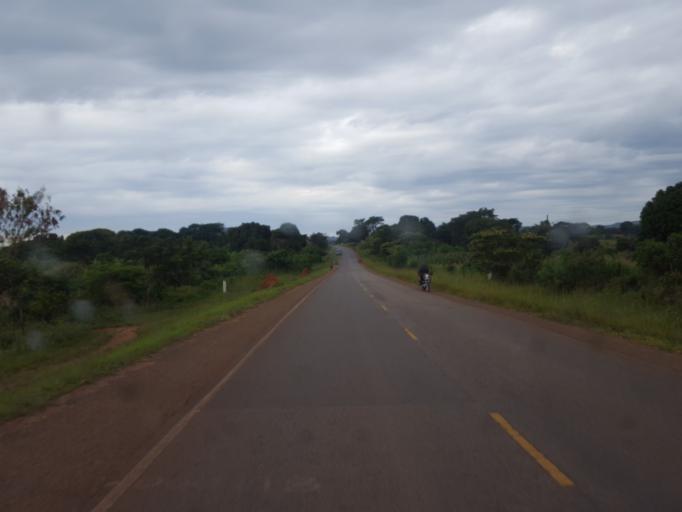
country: UG
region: Central Region
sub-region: Kiboga District
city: Kiboga
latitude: 1.0042
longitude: 31.6978
